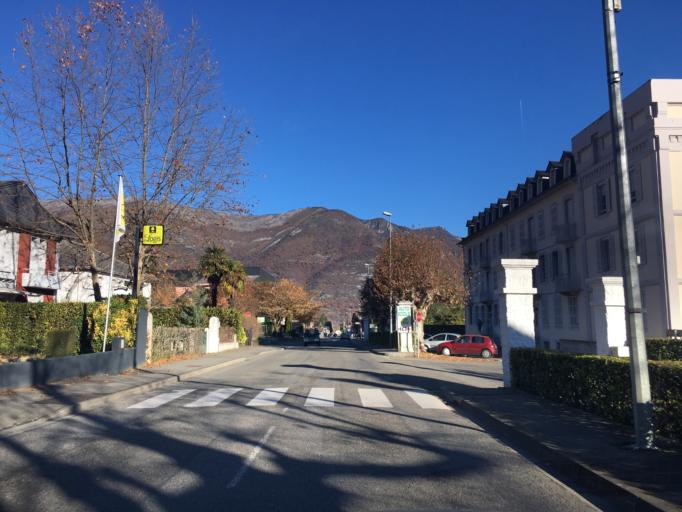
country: FR
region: Midi-Pyrenees
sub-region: Departement des Hautes-Pyrenees
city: Argeles-Gazost
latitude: 43.0041
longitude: -0.0989
